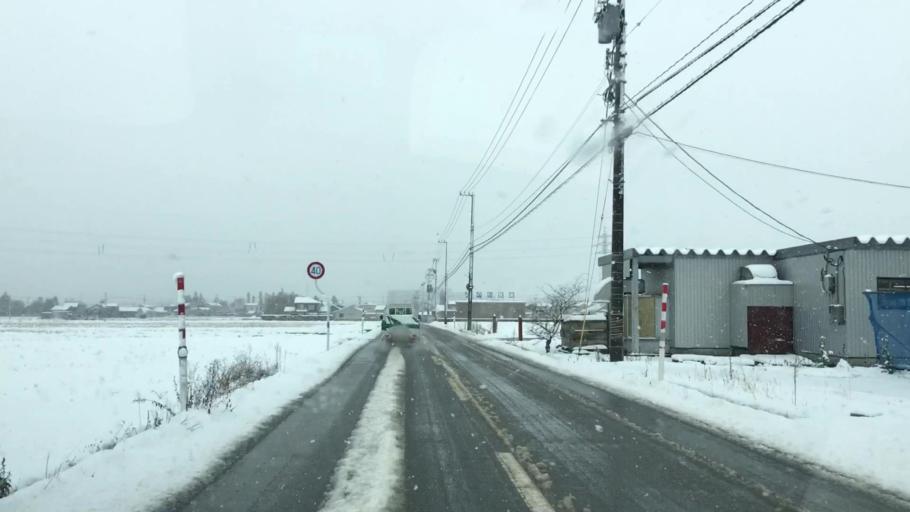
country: JP
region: Toyama
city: Kamiichi
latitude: 36.6894
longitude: 137.3364
